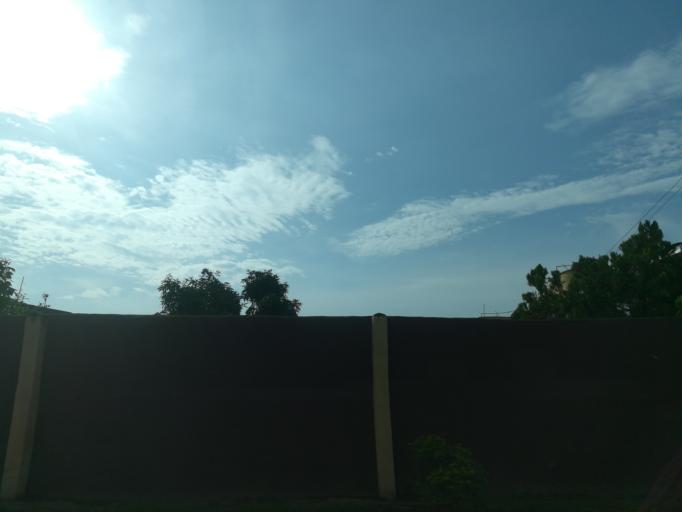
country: NG
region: Lagos
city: Ojota
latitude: 6.6023
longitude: 3.4197
